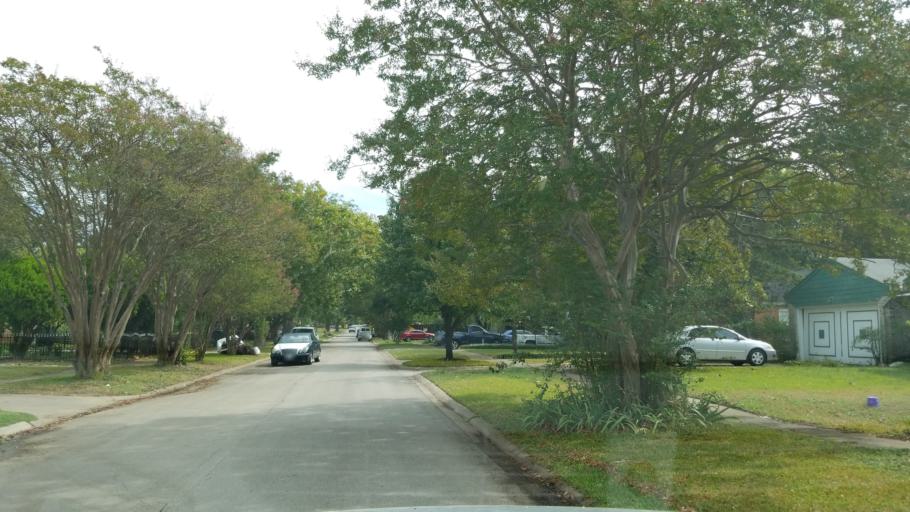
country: US
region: Texas
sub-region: Dallas County
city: Dallas
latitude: 32.7736
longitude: -96.7174
